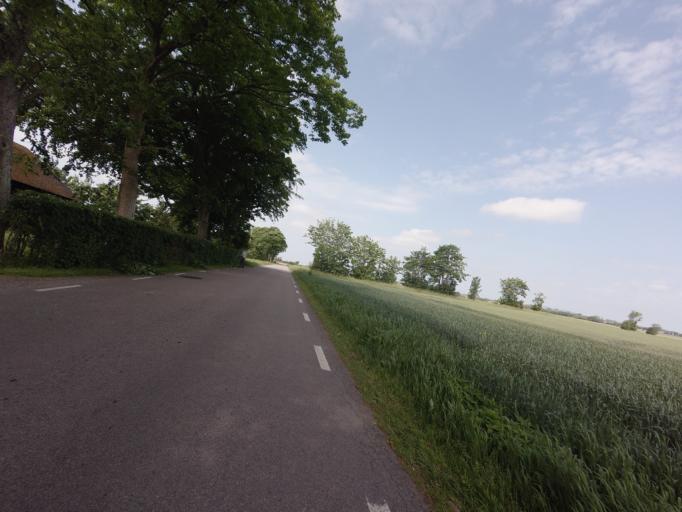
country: SE
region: Skane
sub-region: Hoganas Kommun
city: Hoganas
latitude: 56.1881
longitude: 12.6377
